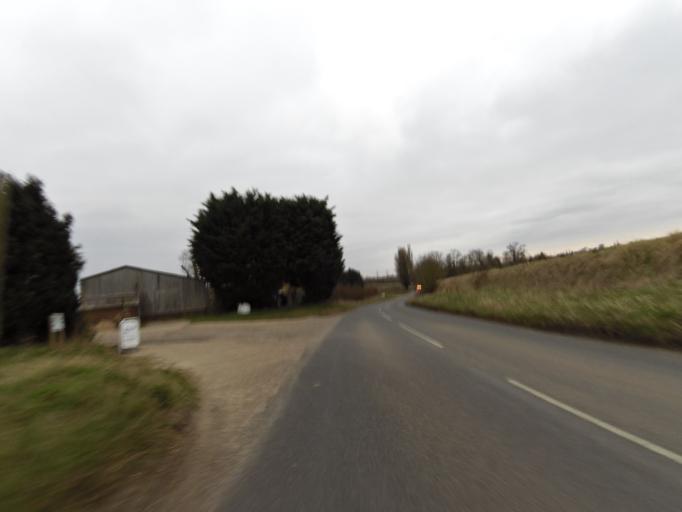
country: GB
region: England
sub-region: Suffolk
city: Ipswich
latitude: 52.1033
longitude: 1.1536
